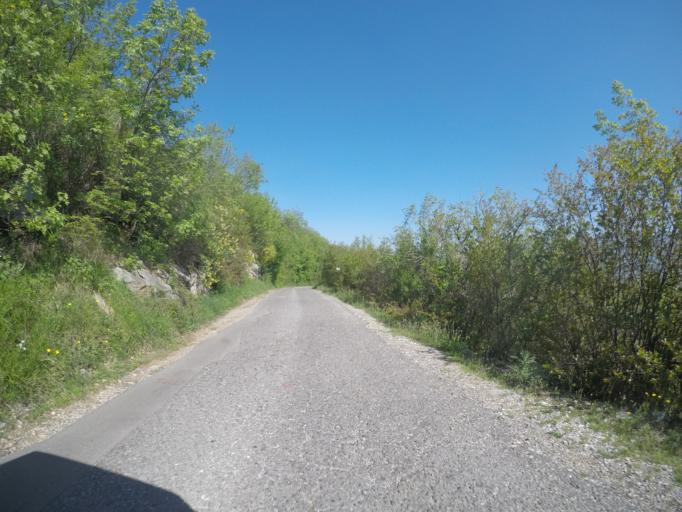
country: ME
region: Danilovgrad
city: Danilovgrad
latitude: 42.5166
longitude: 19.0980
